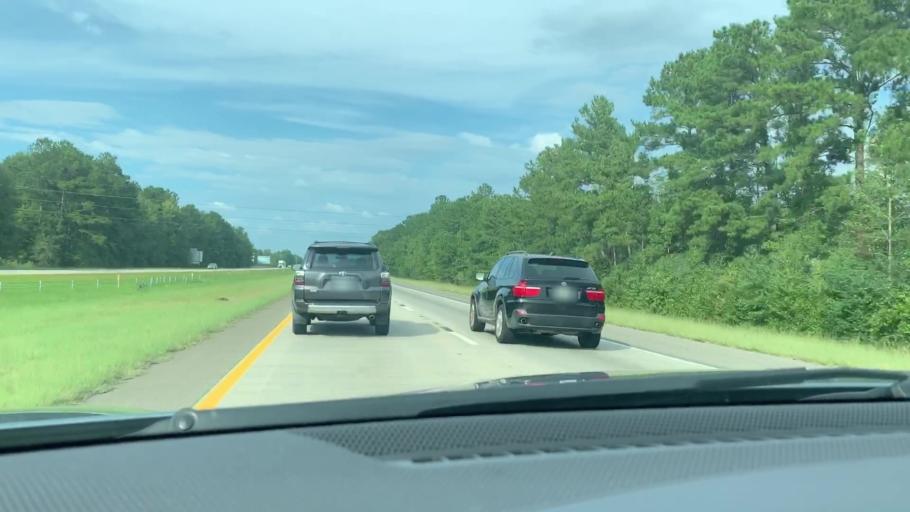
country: US
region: South Carolina
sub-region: Colleton County
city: Walterboro
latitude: 32.9488
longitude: -80.6825
